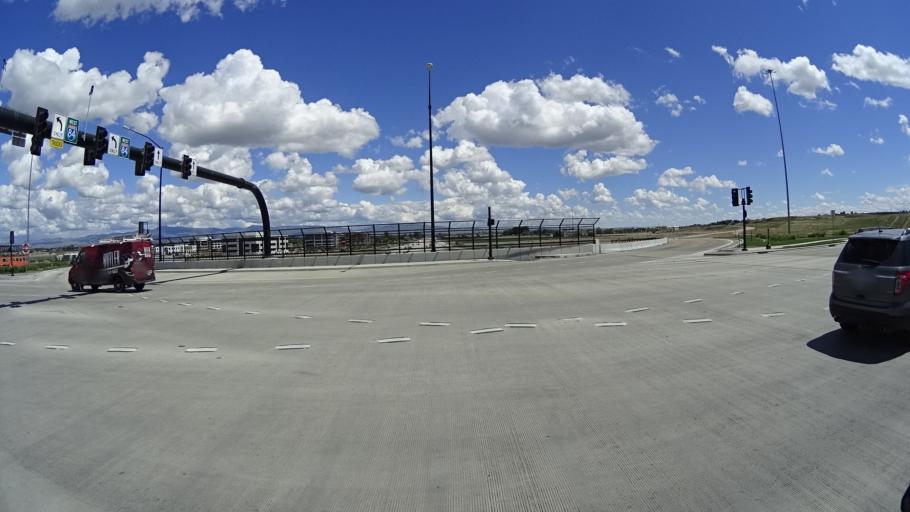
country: US
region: Idaho
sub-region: Ada County
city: Meridian
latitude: 43.5932
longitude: -116.4343
